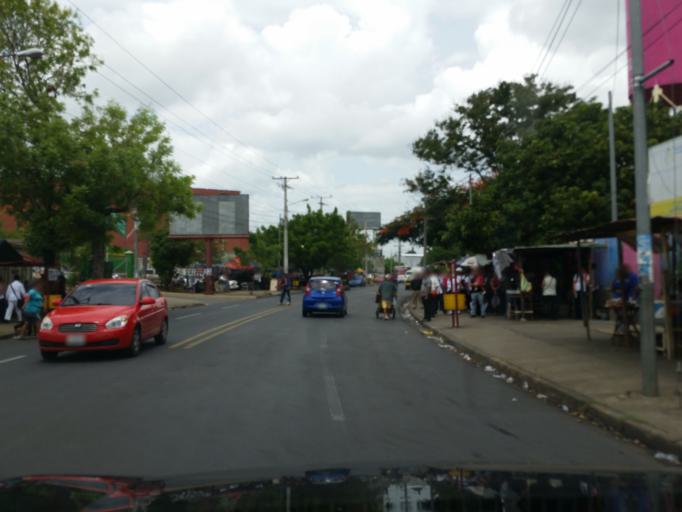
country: NI
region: Managua
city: Managua
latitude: 12.1487
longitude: -86.2494
